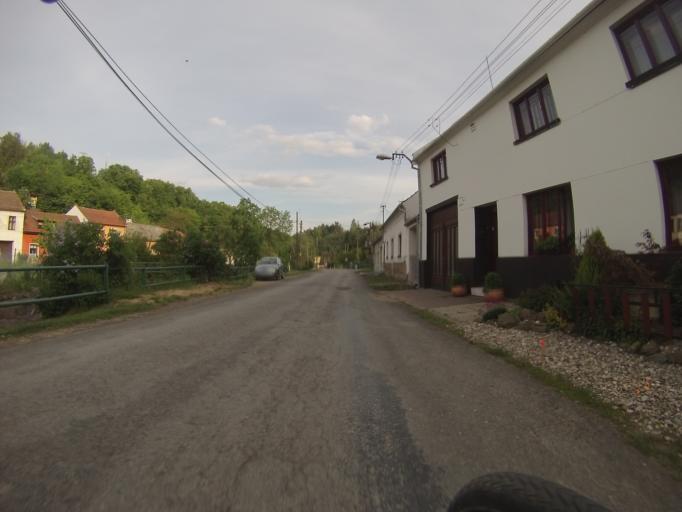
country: CZ
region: Olomoucky
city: Pteni
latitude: 49.4698
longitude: 16.9694
